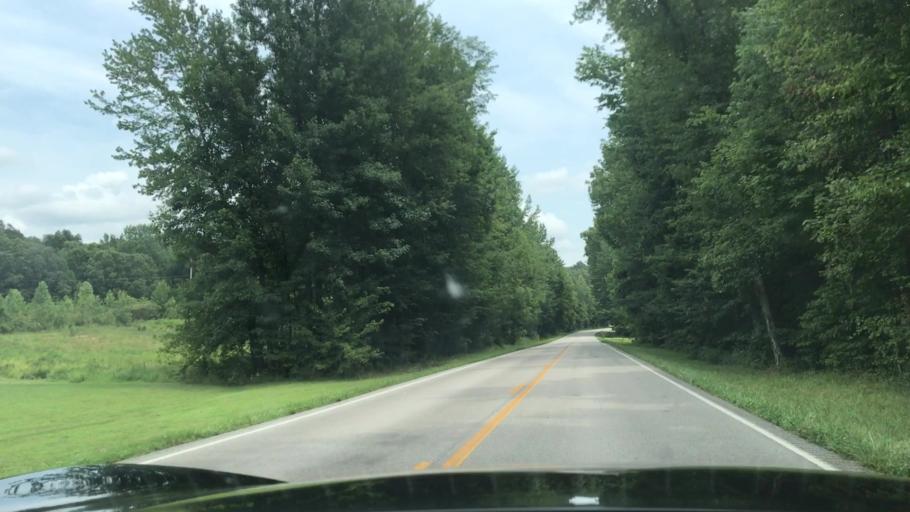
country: US
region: Kentucky
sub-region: Butler County
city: Morgantown
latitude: 37.1753
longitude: -86.8423
